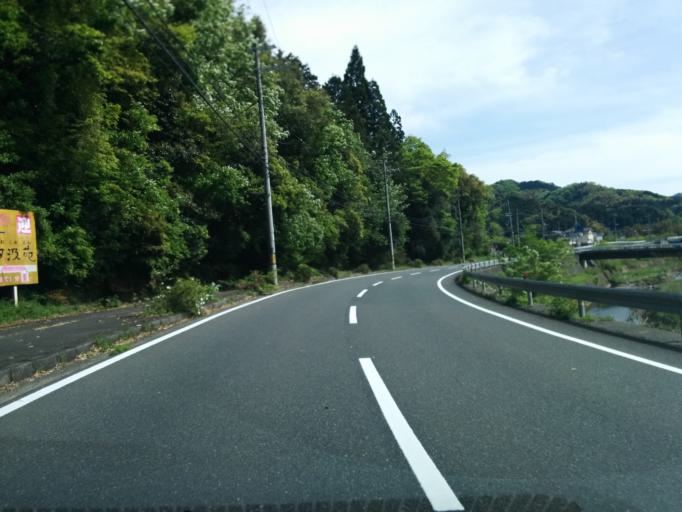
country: JP
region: Kyoto
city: Miyazu
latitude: 35.4283
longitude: 135.2153
